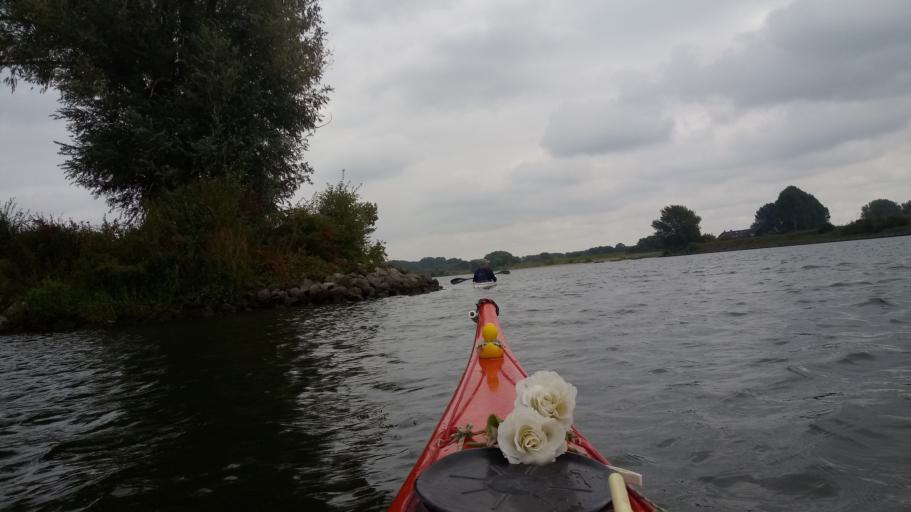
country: NL
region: Gelderland
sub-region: Gemeente Maasdriel
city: Hedel
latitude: 51.7344
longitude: 5.2491
